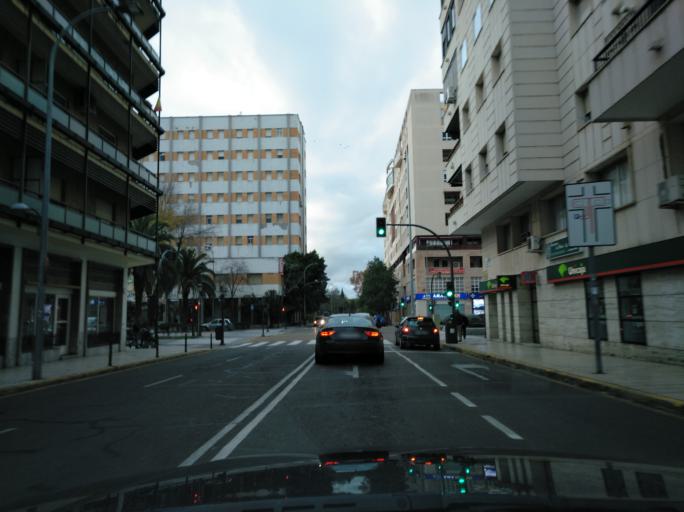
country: ES
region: Extremadura
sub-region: Provincia de Badajoz
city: Badajoz
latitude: 38.8762
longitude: -6.9760
